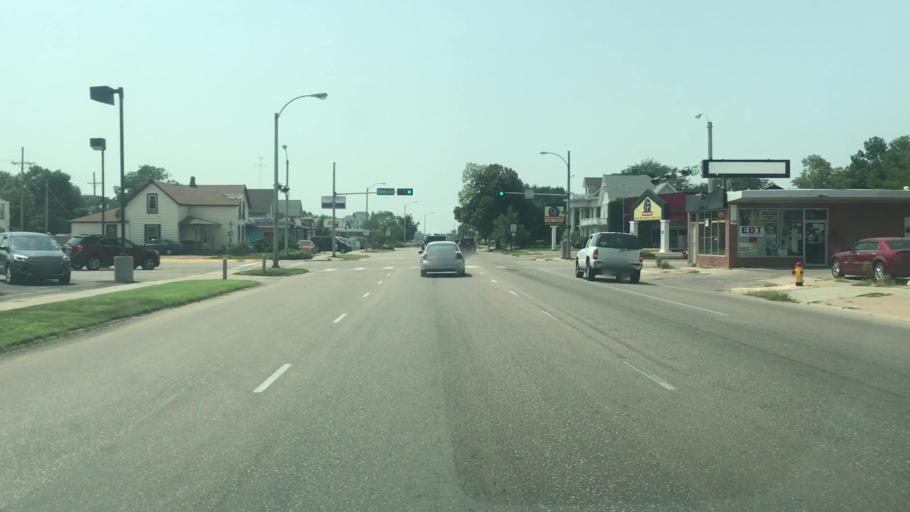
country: US
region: Nebraska
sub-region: Hall County
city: Grand Island
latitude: 40.9221
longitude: -98.3465
